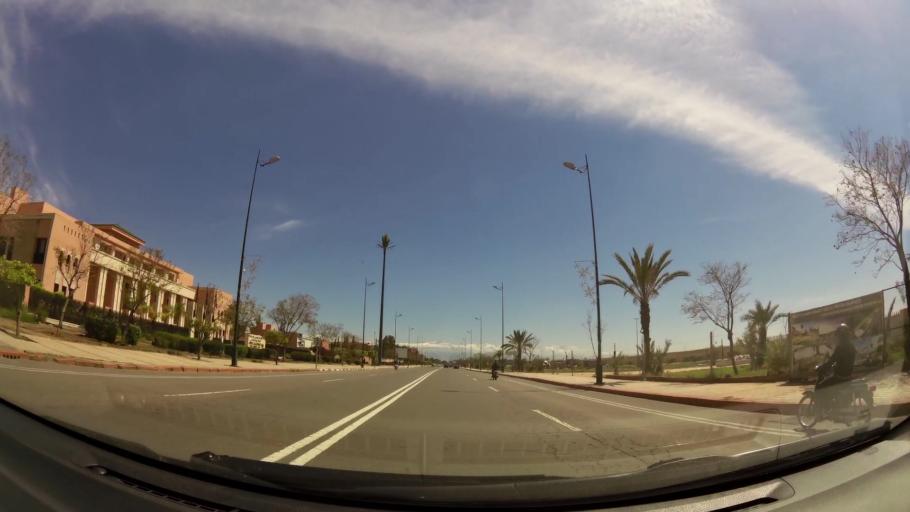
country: MA
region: Marrakech-Tensift-Al Haouz
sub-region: Marrakech
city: Marrakesh
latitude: 31.6109
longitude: -7.9741
